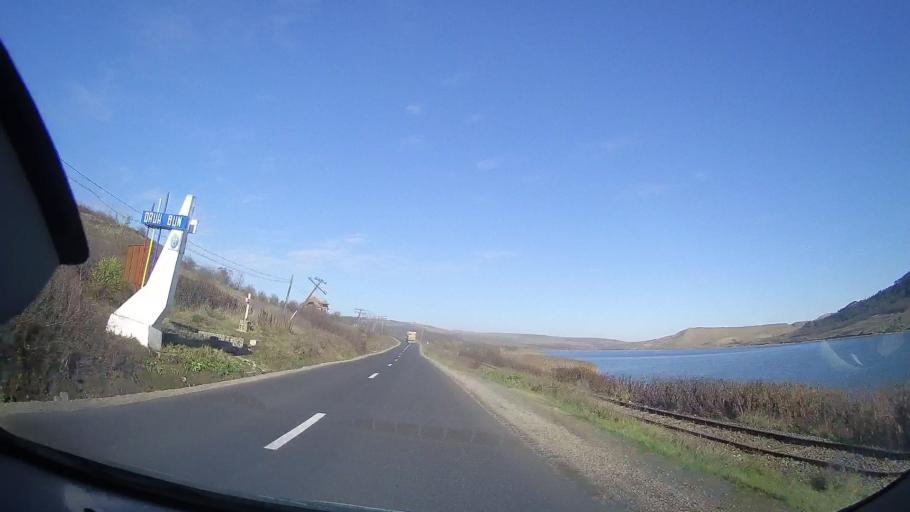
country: RO
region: Mures
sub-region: Comuna Zau De Campie
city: Zau de Campie
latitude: 46.6243
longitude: 24.1325
